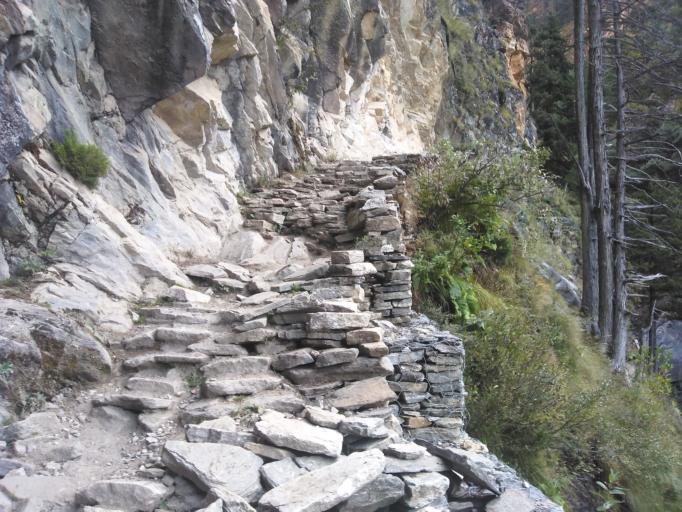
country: NP
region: Western Region
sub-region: Dhawalagiri Zone
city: Jomsom
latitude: 28.9231
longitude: 83.0346
